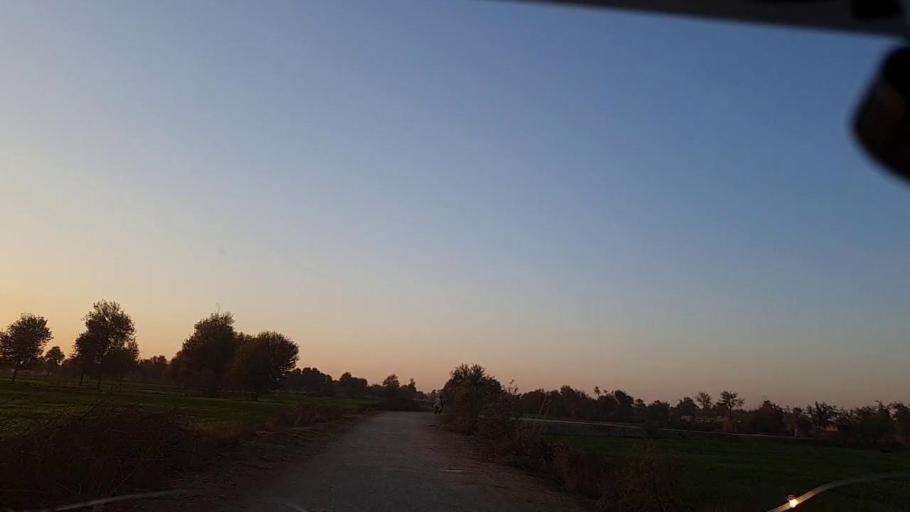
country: PK
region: Sindh
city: Adilpur
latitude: 27.8388
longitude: 69.2989
